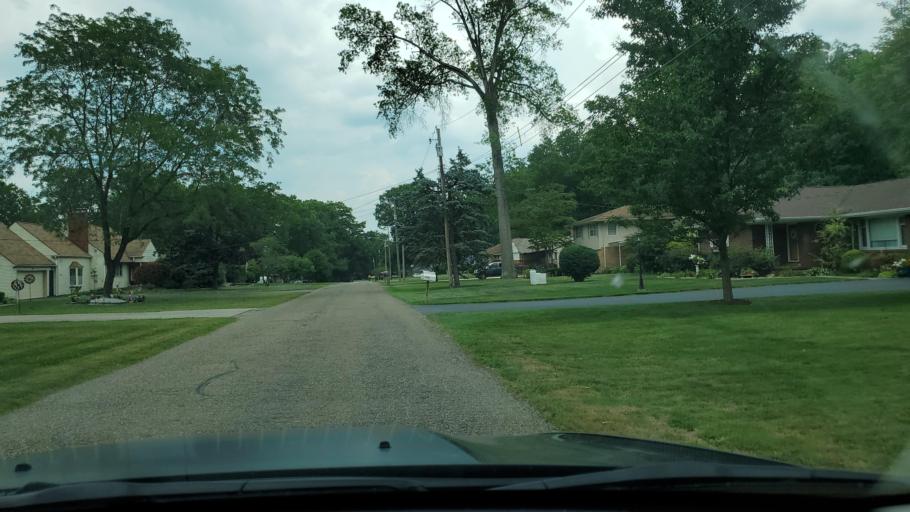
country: US
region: Ohio
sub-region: Trumbull County
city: Bolindale
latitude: 41.2314
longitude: -80.7709
